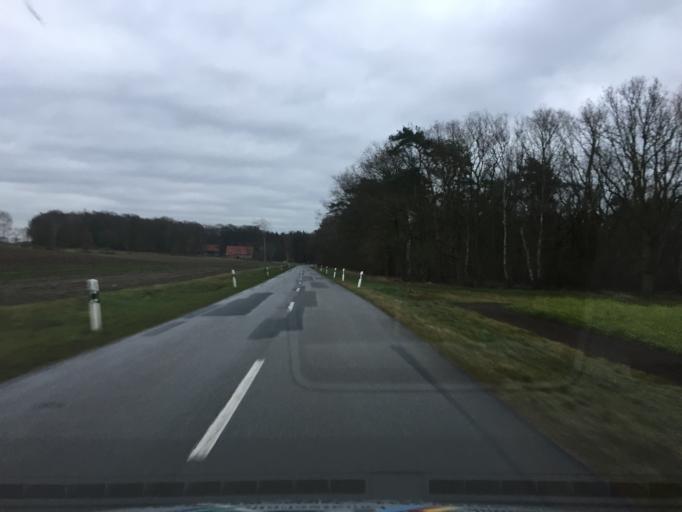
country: DE
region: Lower Saxony
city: Borstel
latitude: 52.6516
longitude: 8.9909
